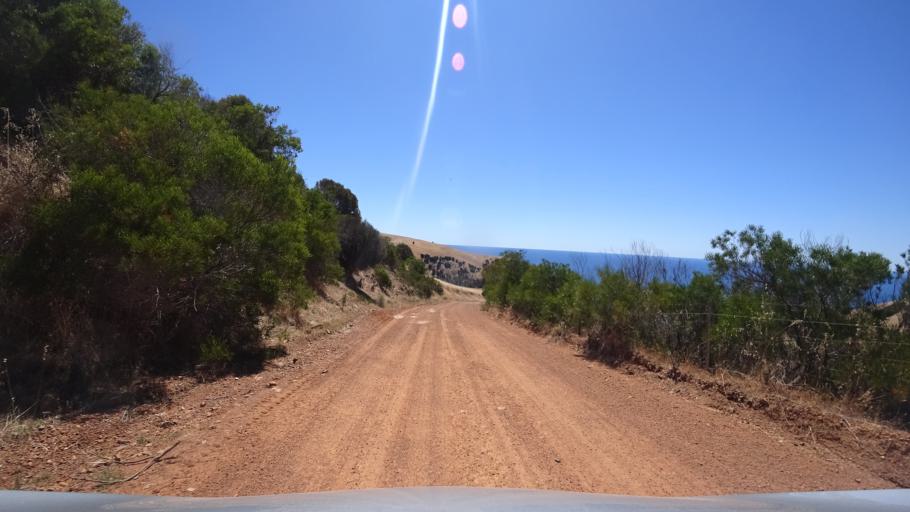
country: AU
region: South Australia
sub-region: Kangaroo Island
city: Kingscote
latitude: -35.6777
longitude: 136.9750
